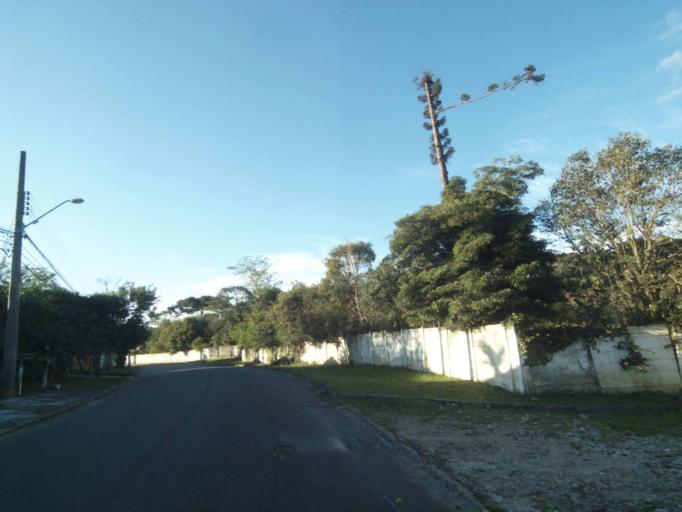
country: BR
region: Parana
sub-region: Curitiba
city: Curitiba
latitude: -25.3741
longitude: -49.2506
